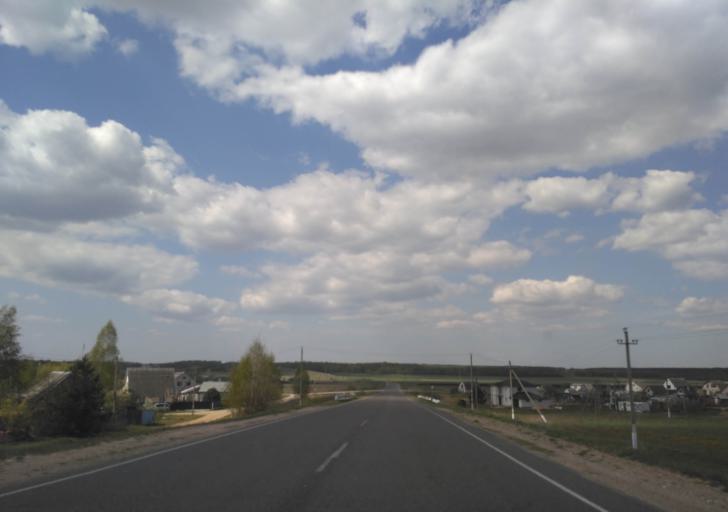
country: BY
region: Minsk
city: Vilyeyka
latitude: 54.5176
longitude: 26.9795
